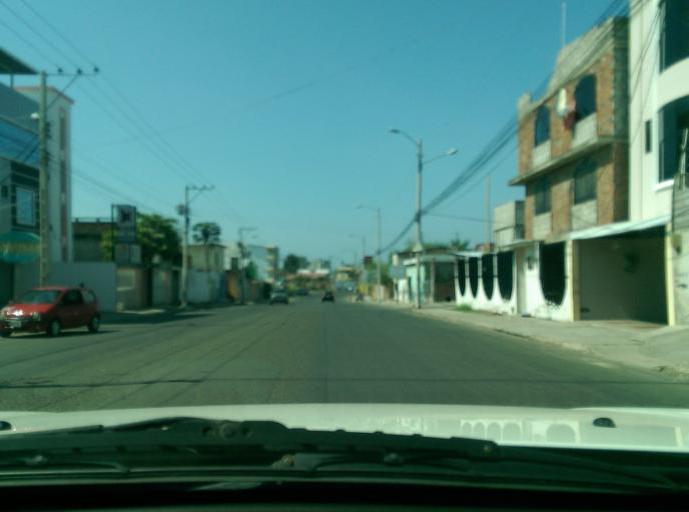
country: EC
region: Manabi
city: Manta
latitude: -0.9520
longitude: -80.7429
